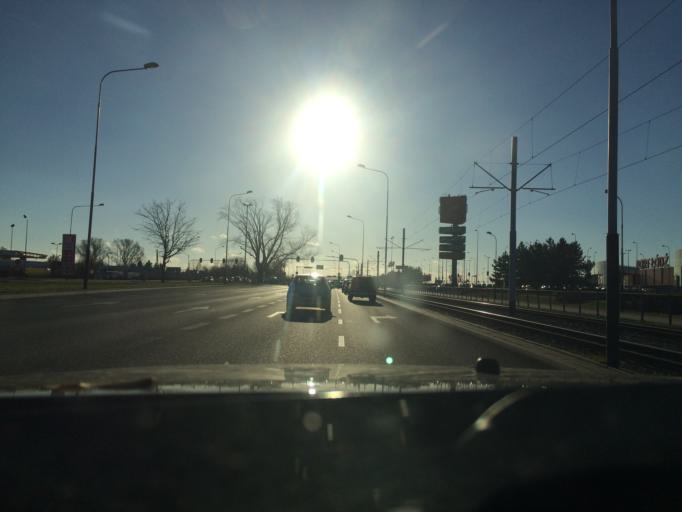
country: PL
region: Lodz Voivodeship
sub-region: Powiat pabianicki
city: Ksawerow
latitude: 51.7044
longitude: 19.4198
